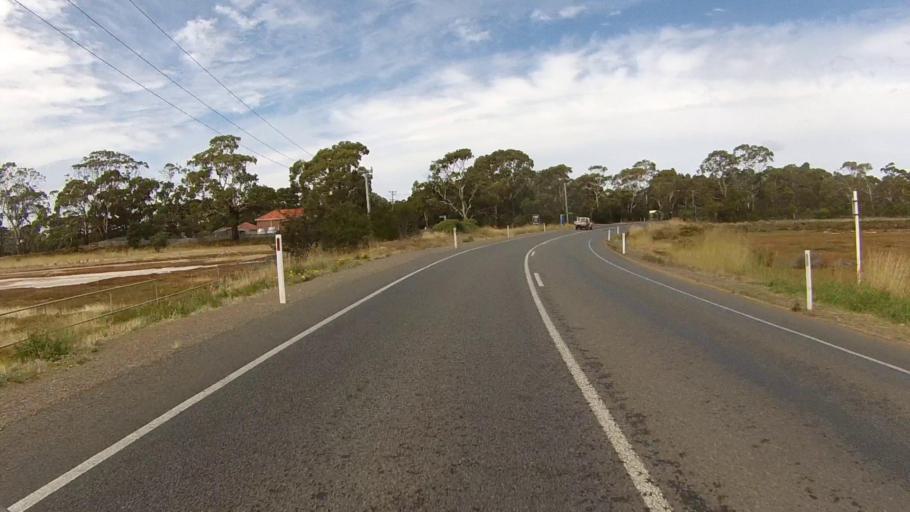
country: AU
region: Tasmania
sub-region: Clarence
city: Sandford
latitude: -42.9270
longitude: 147.4916
